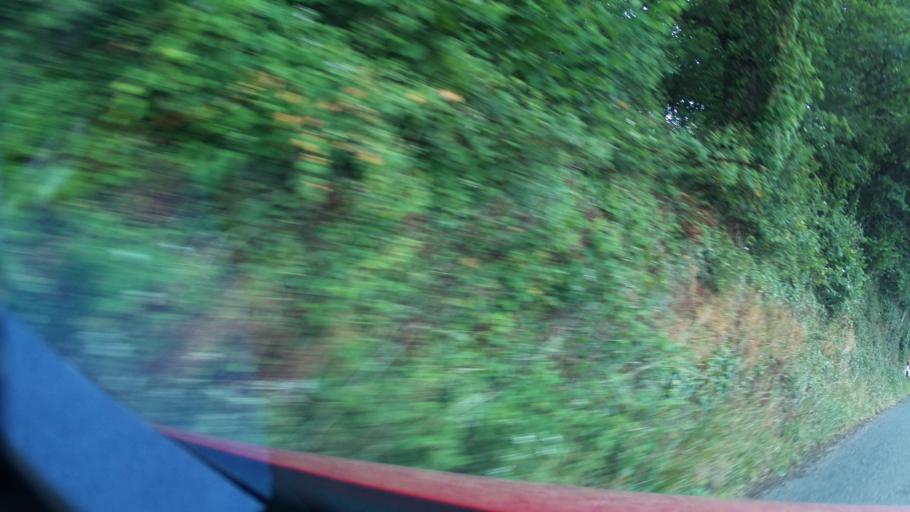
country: GB
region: England
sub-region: Devon
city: Chudleigh
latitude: 50.6096
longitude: -3.6208
